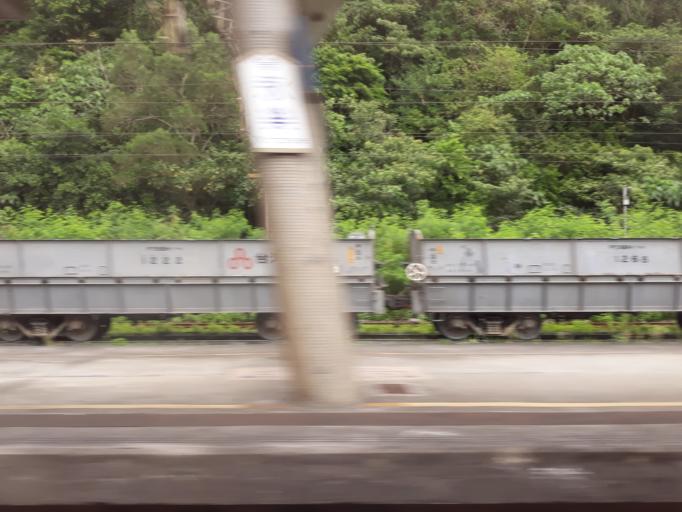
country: TW
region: Taiwan
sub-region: Yilan
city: Yilan
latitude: 24.5681
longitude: 121.8442
